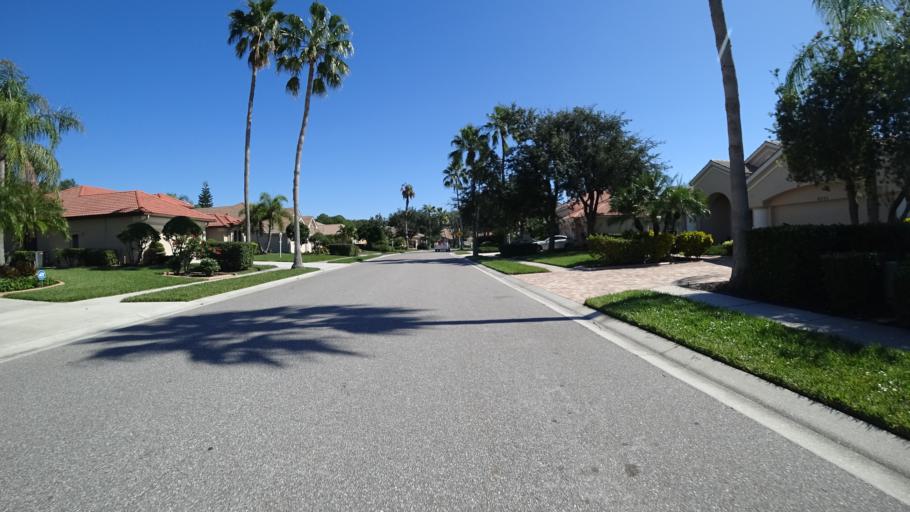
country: US
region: Florida
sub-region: Sarasota County
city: The Meadows
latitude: 27.4017
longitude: -82.4251
